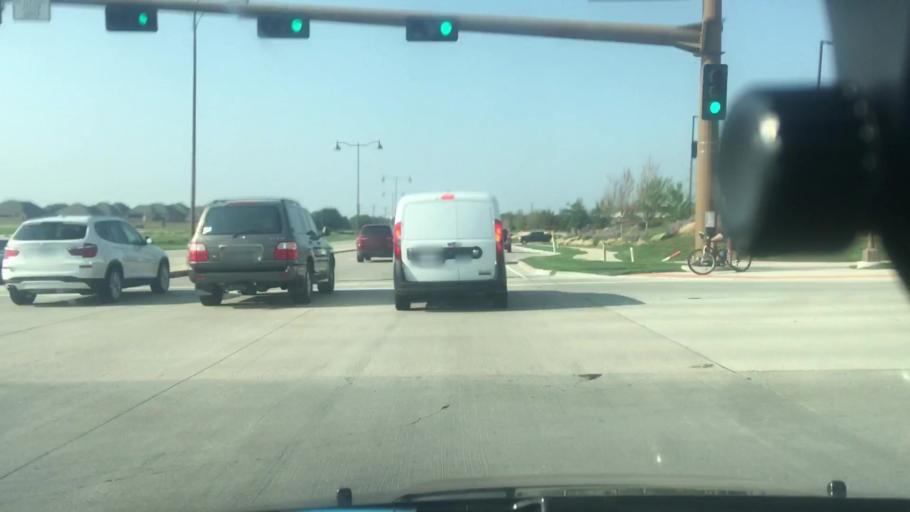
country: US
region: Texas
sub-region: Collin County
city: Prosper
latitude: 33.2481
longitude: -96.7848
